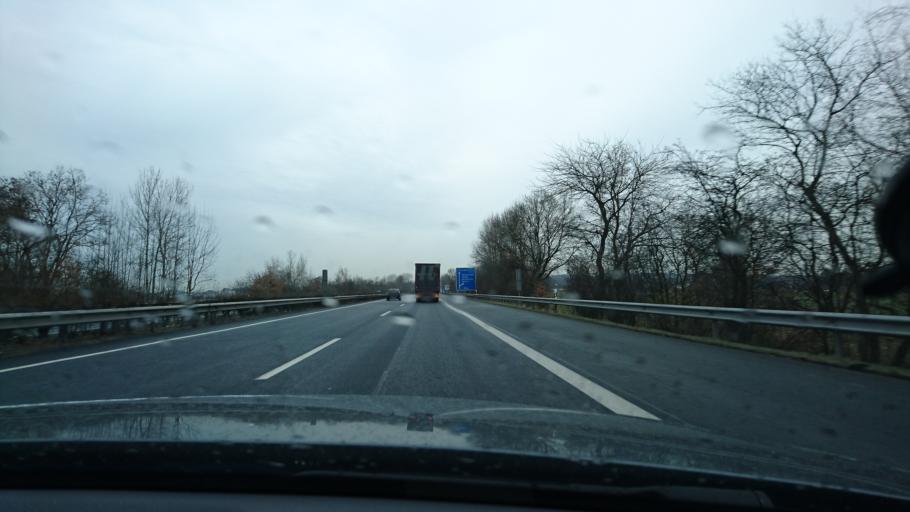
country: DE
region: Lower Saxony
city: Neuenkirchen
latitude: 52.4852
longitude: 8.0668
